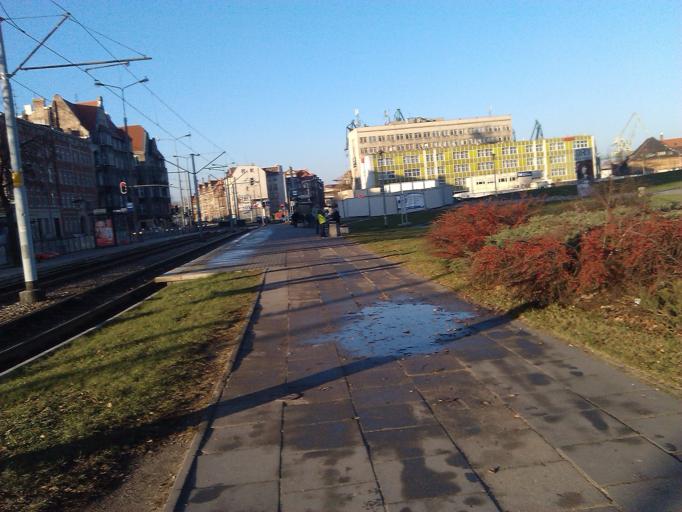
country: PL
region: Pomeranian Voivodeship
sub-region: Gdansk
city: Gdansk
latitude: 54.3601
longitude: 18.6483
